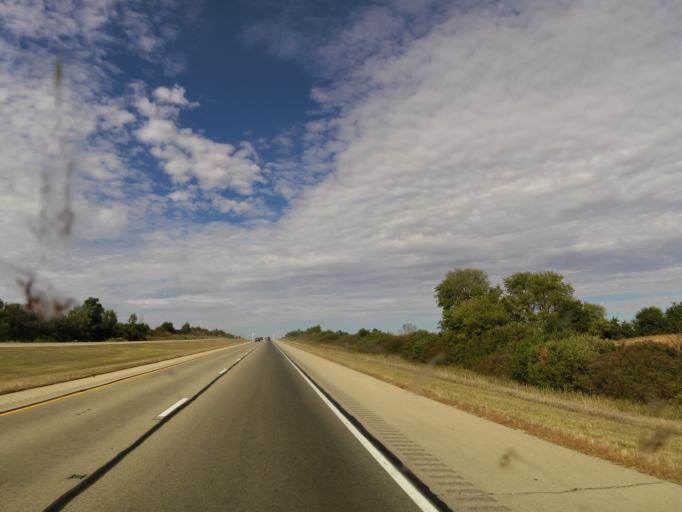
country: US
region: Illinois
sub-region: LaSalle County
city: Mendota
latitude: 41.6331
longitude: -89.0608
